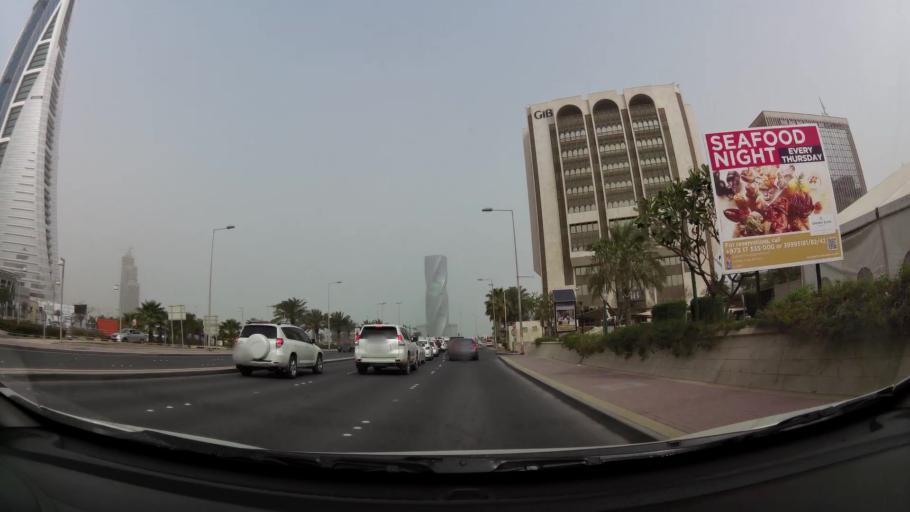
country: BH
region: Manama
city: Manama
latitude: 26.2402
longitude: 50.5838
